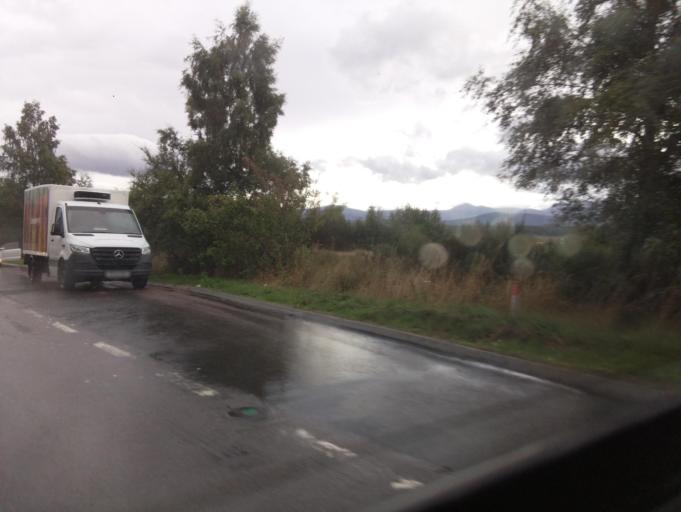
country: GB
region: Scotland
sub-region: Highland
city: Grantown on Spey
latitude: 57.2813
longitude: -3.6783
